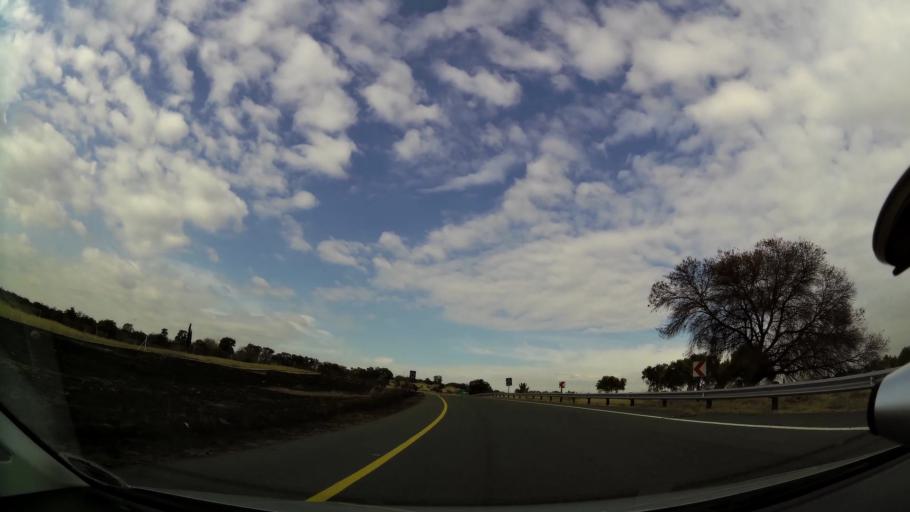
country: ZA
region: Orange Free State
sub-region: Fezile Dabi District Municipality
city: Kroonstad
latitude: -27.6855
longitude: 27.2436
